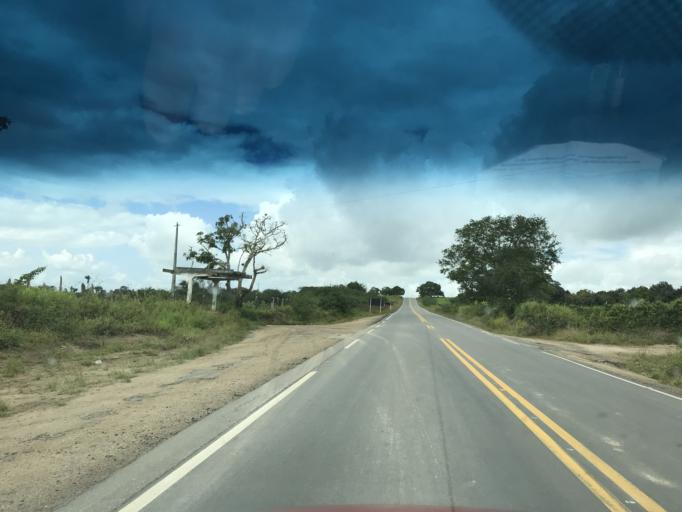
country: BR
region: Bahia
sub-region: Conceicao Do Almeida
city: Conceicao do Almeida
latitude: -12.6818
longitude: -39.2551
